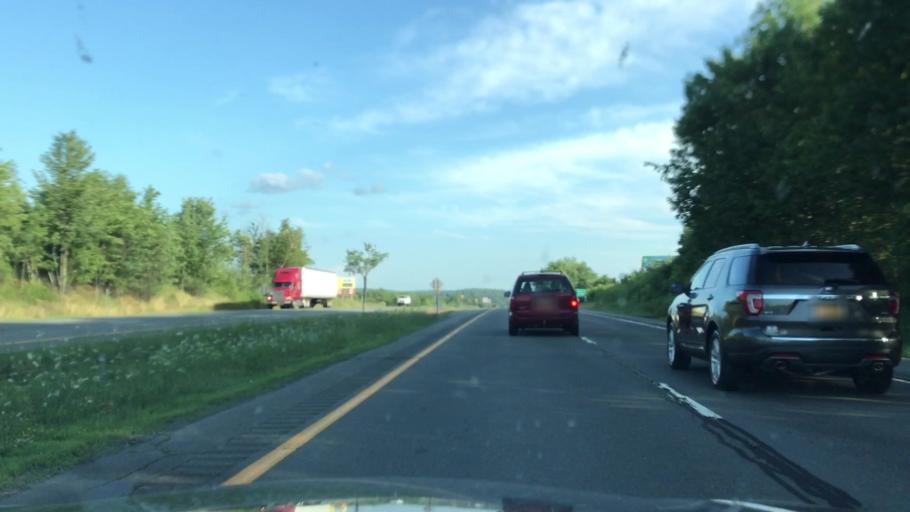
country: US
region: New York
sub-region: Sullivan County
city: Liberty
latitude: 41.7406
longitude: -74.7321
